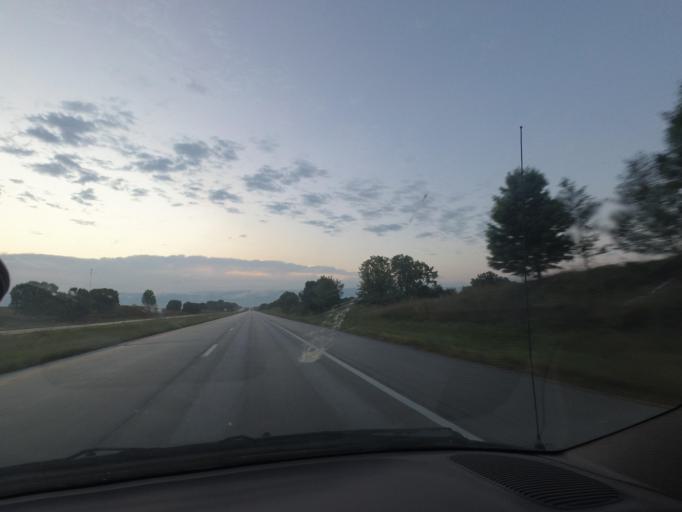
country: US
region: Missouri
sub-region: Macon County
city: Macon
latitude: 39.7582
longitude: -92.5475
